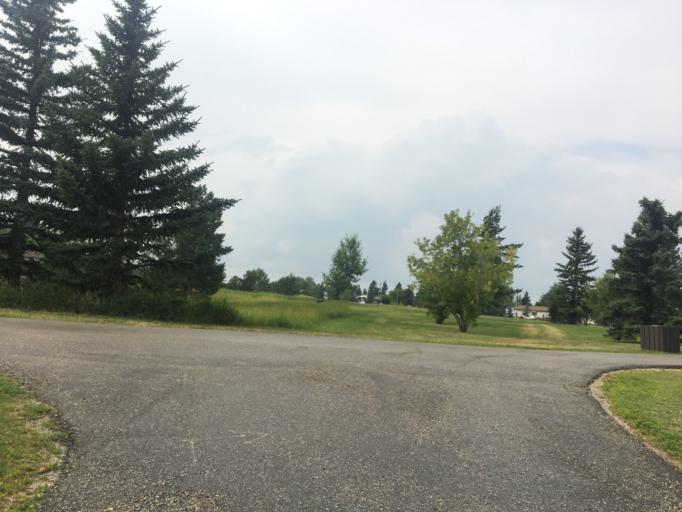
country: CA
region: Alberta
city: Grande Prairie
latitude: 55.1763
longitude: -118.8079
